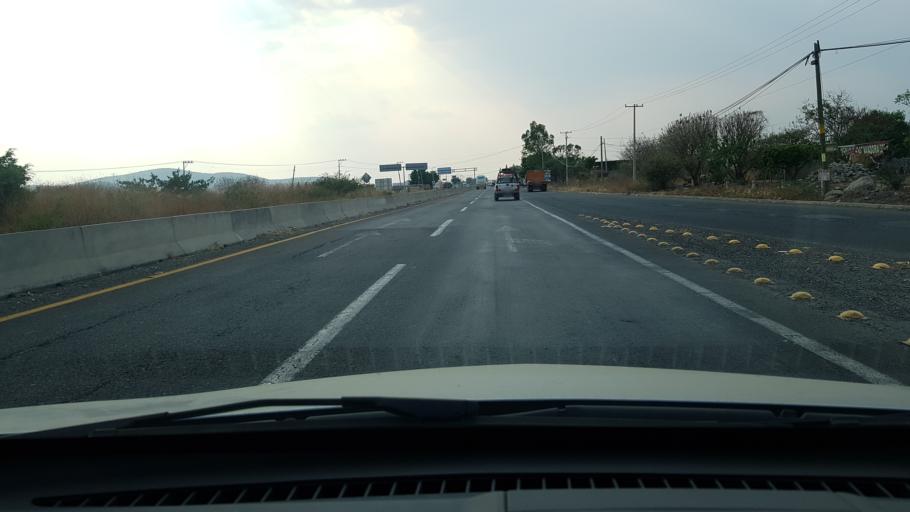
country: MX
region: Morelos
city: Amayuca
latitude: 18.7317
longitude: -98.8131
